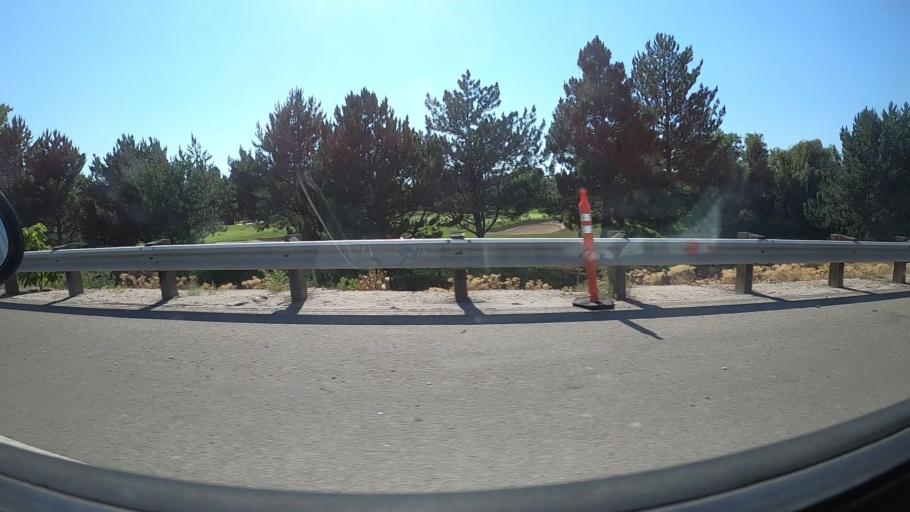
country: US
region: Idaho
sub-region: Ada County
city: Eagle
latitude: 43.6683
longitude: -116.3546
